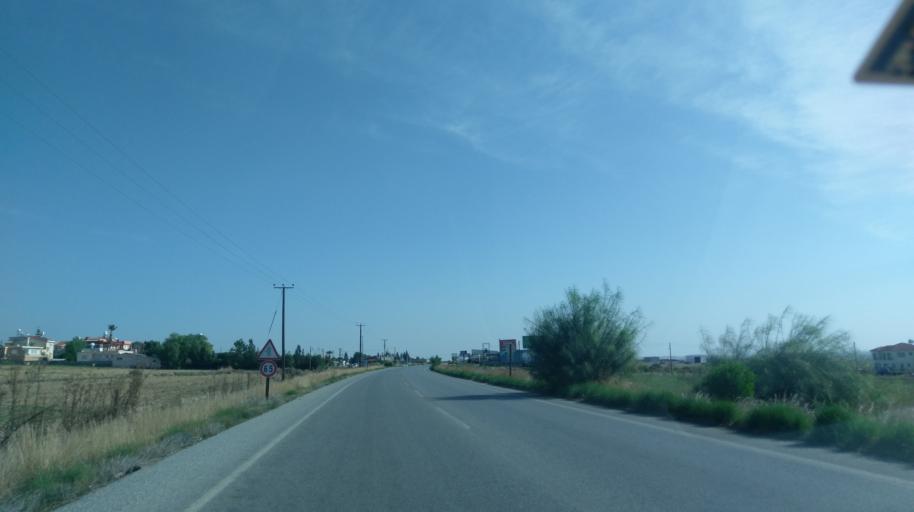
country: CY
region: Ammochostos
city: Lefkonoiko
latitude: 35.2422
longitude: 33.5955
